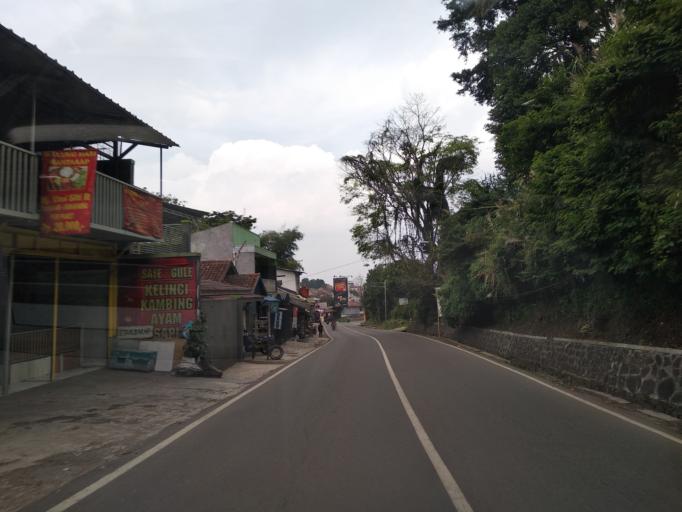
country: ID
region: West Java
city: Lembang
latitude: -6.8293
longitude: 107.6070
